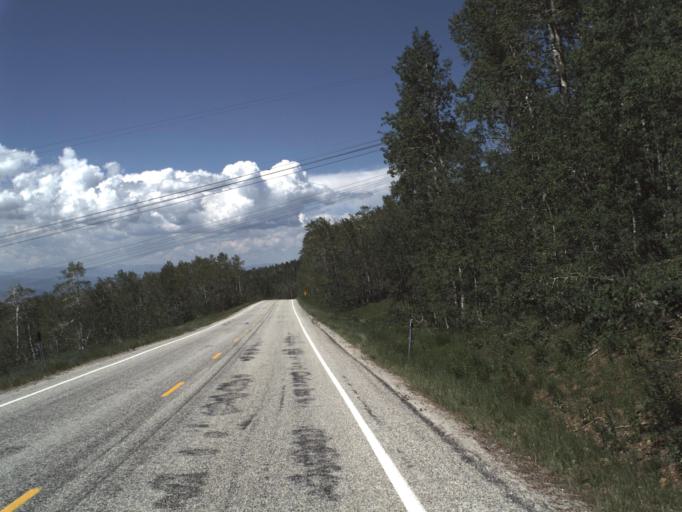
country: US
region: Utah
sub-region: Weber County
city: Wolf Creek
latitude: 41.4067
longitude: -111.5282
